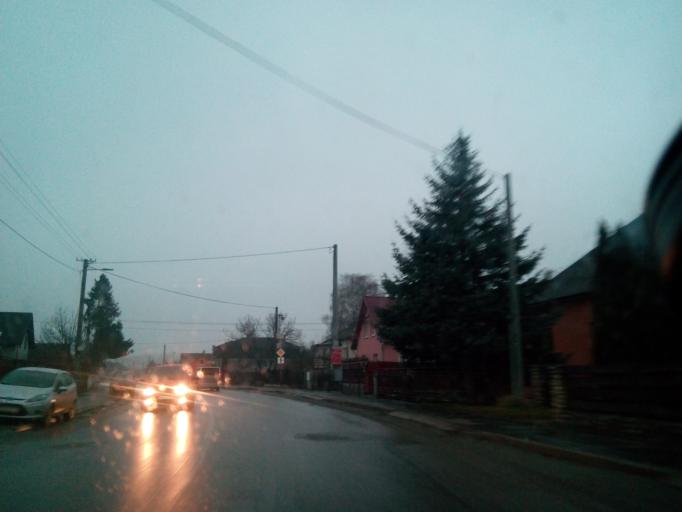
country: SK
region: Presovsky
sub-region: Okres Presov
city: Presov
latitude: 49.0418
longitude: 21.2023
